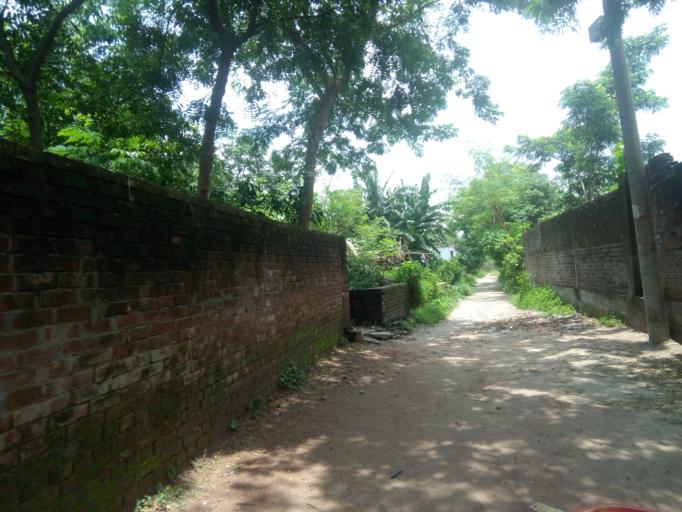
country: BD
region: Dhaka
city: Azimpur
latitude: 23.7394
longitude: 90.3453
